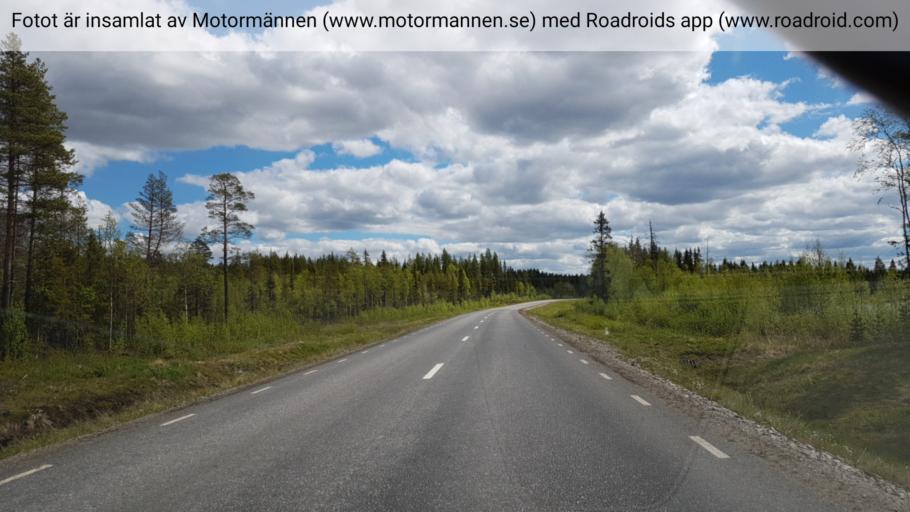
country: SE
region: Vaesterbotten
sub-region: Norsjo Kommun
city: Norsjoe
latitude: 64.8975
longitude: 19.5666
